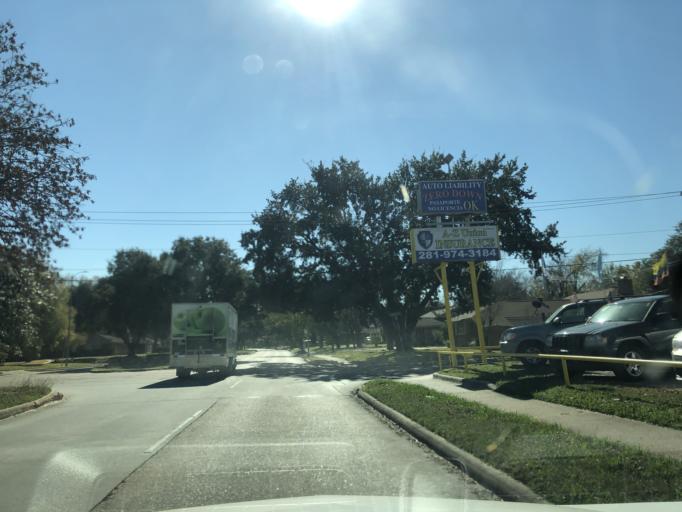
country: US
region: Texas
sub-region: Harris County
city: Bellaire
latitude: 29.6925
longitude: -95.4931
